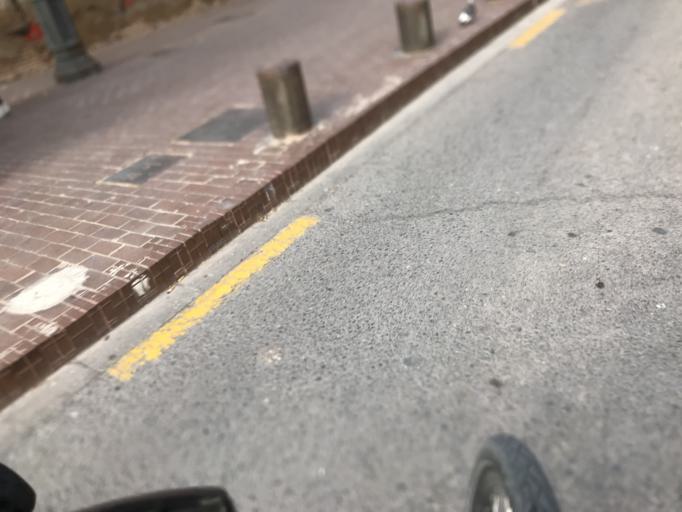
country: ES
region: Valencia
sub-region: Provincia de Valencia
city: Valencia
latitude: 39.4741
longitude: -0.3806
